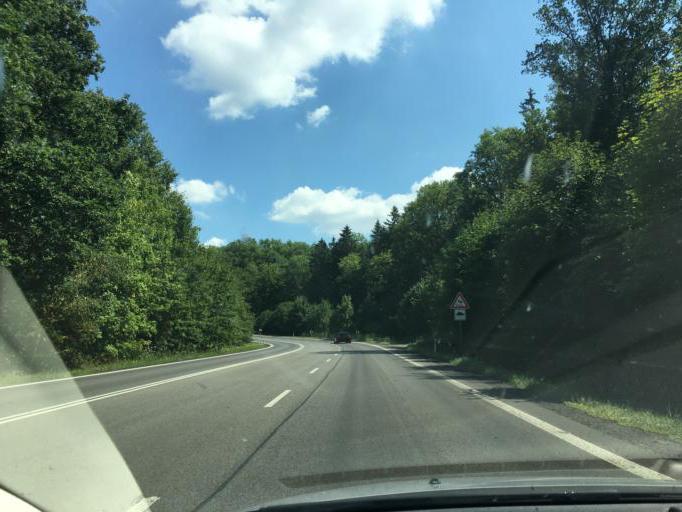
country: CZ
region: Ustecky
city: Benesov nad Ploucnici
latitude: 50.7879
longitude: 14.2758
